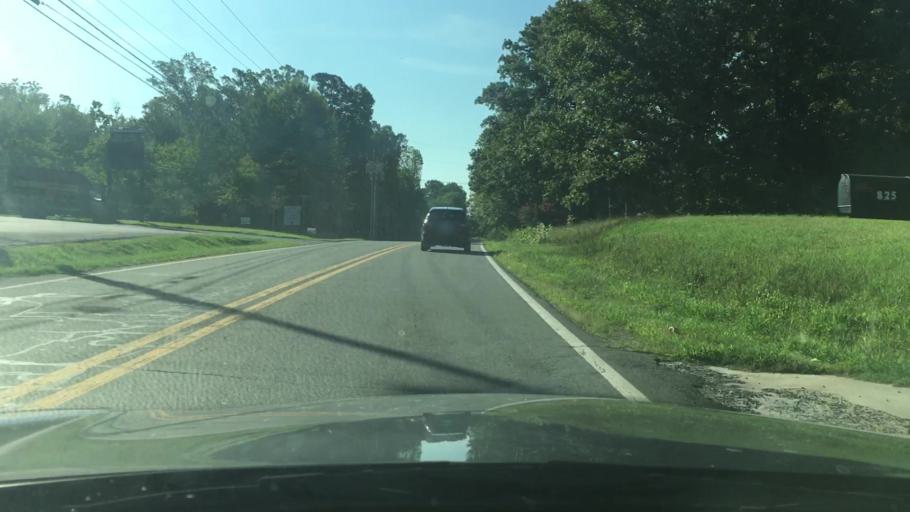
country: US
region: North Carolina
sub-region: Alamance County
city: Burlington
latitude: 36.0726
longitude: -79.4386
